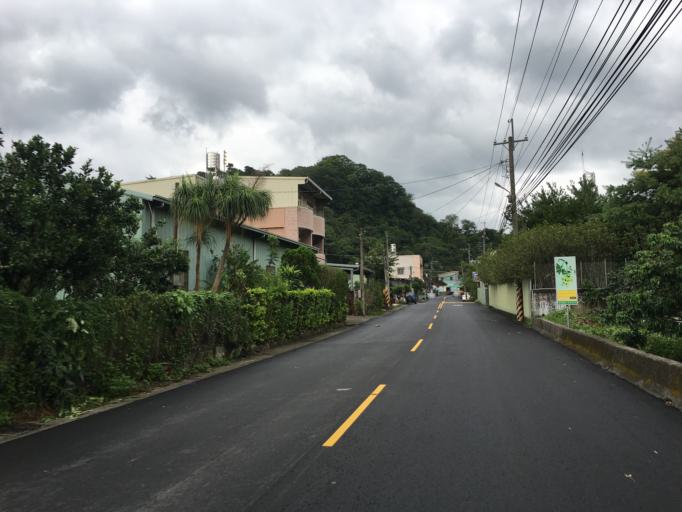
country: TW
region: Taiwan
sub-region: Taichung City
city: Taichung
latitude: 24.0700
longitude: 120.7325
